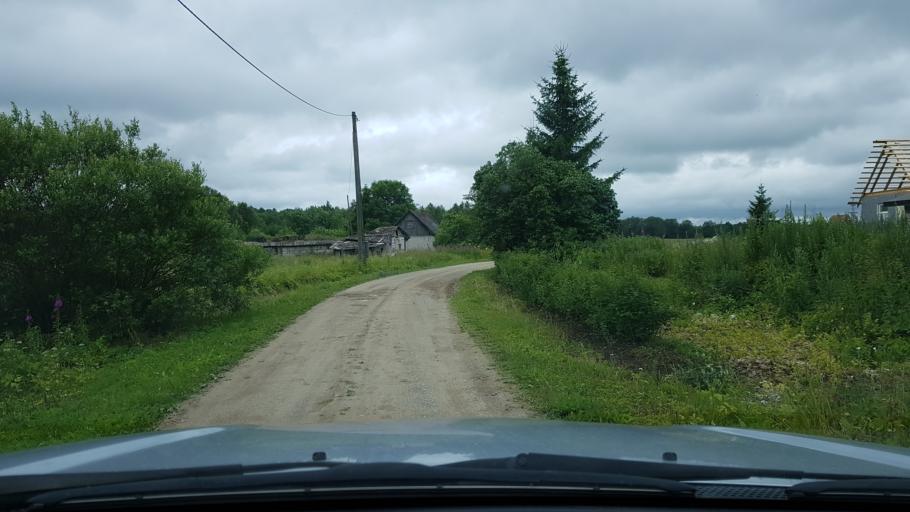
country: EE
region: Ida-Virumaa
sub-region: Narva-Joesuu linn
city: Narva-Joesuu
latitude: 59.3484
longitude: 28.0194
